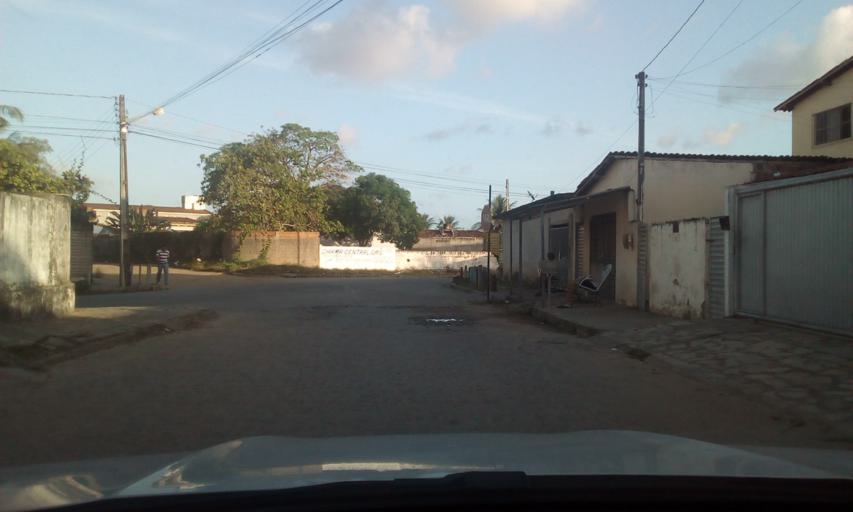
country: BR
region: Paraiba
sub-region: Conde
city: Conde
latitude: -7.2015
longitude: -34.8593
